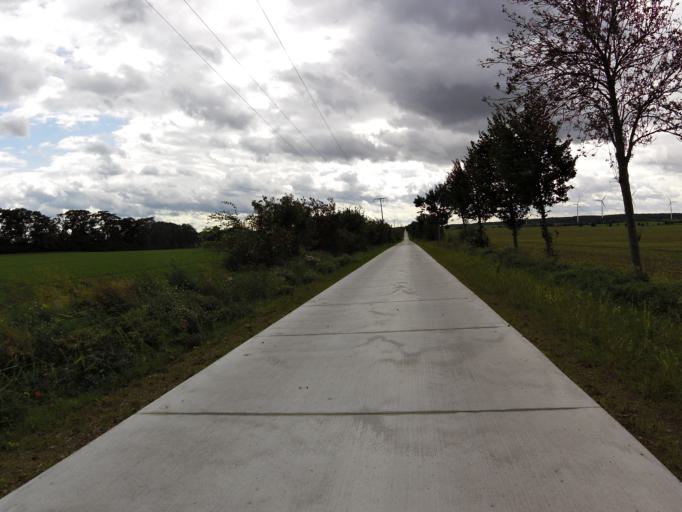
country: DE
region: Saxony-Anhalt
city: Arneburg
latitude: 52.6599
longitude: 12.0043
